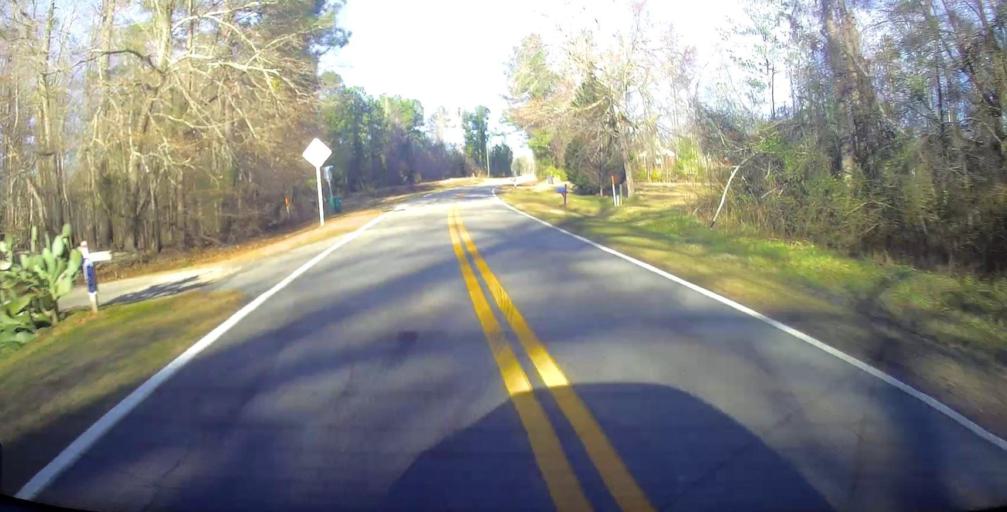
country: US
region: Georgia
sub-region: Crawford County
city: Roberta
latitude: 32.7592
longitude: -84.1322
